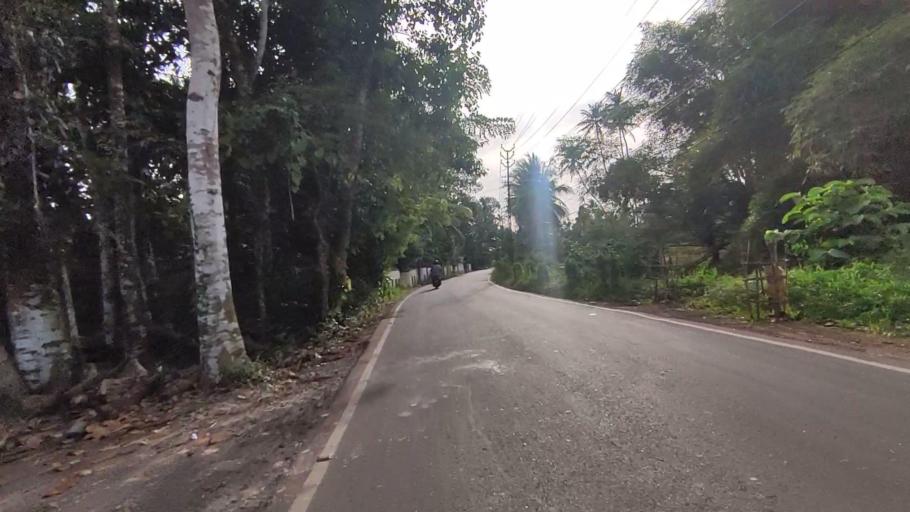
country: IN
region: Kerala
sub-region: Kottayam
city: Kottayam
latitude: 9.6023
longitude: 76.4999
